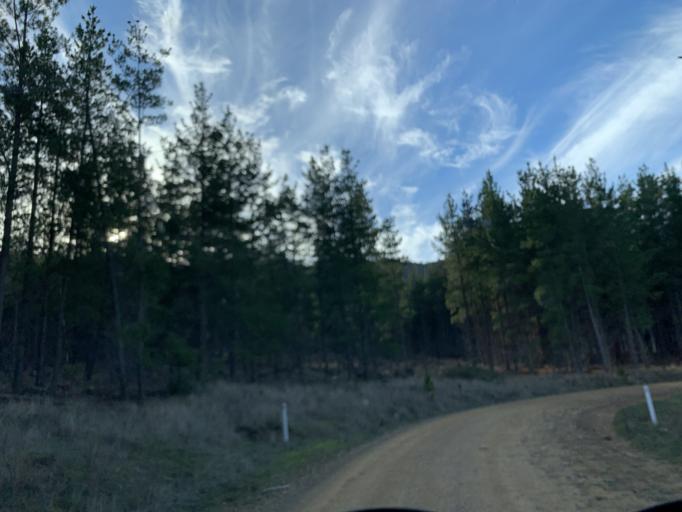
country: AU
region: Victoria
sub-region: Mansfield
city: Mansfield
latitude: -36.9332
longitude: 146.0924
